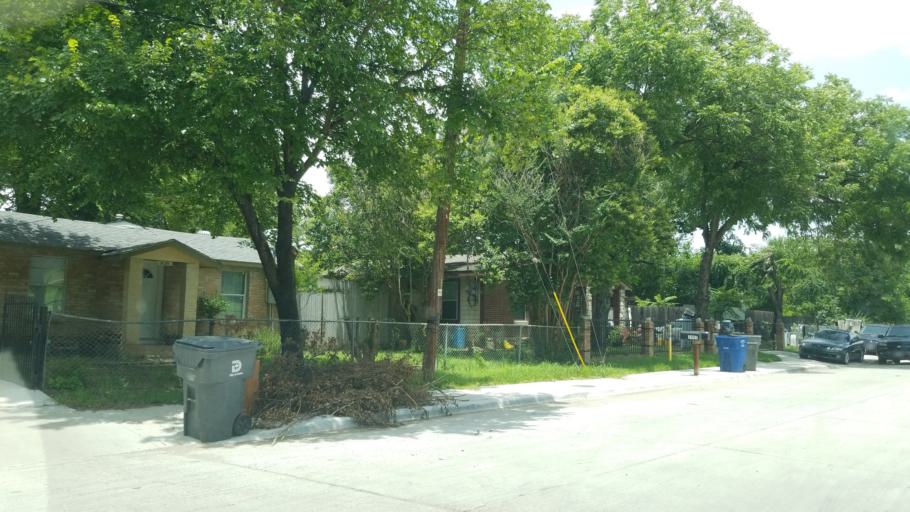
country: US
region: Texas
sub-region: Dallas County
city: Cockrell Hill
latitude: 32.7892
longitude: -96.8910
